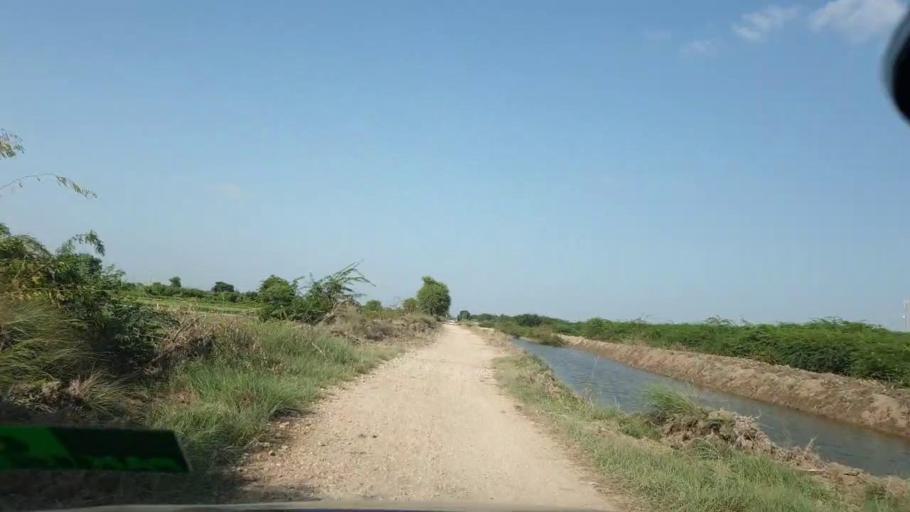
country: PK
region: Sindh
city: Naukot
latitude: 24.7086
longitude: 69.2046
